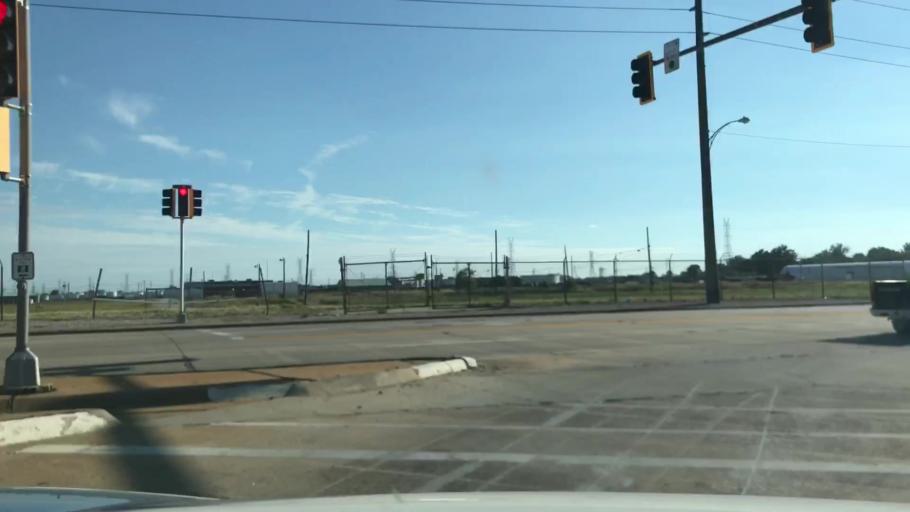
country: US
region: Illinois
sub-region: Madison County
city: Wood River
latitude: 38.8603
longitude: -90.0982
